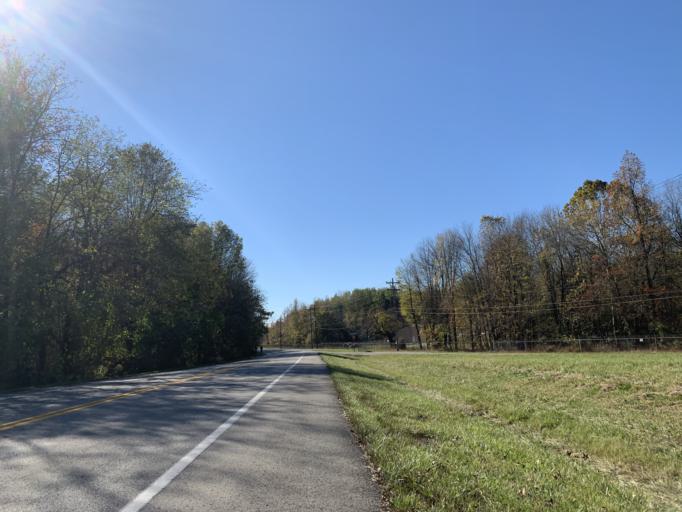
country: US
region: Kentucky
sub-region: Jefferson County
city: Saint Dennis
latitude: 38.1984
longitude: -85.8603
